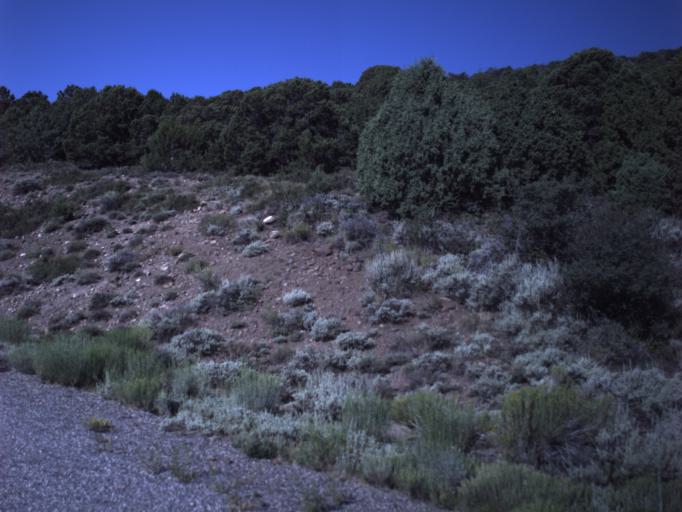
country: US
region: Utah
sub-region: Wayne County
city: Loa
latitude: 38.6133
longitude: -111.4597
